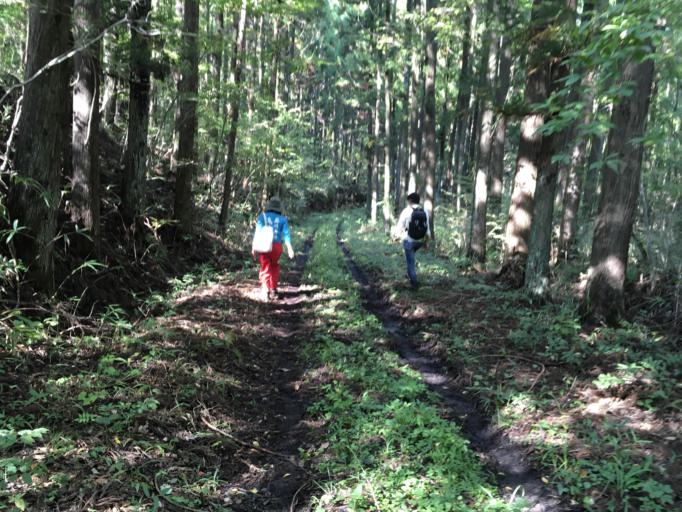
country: JP
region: Iwate
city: Ichinoseki
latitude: 38.8839
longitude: 141.1250
